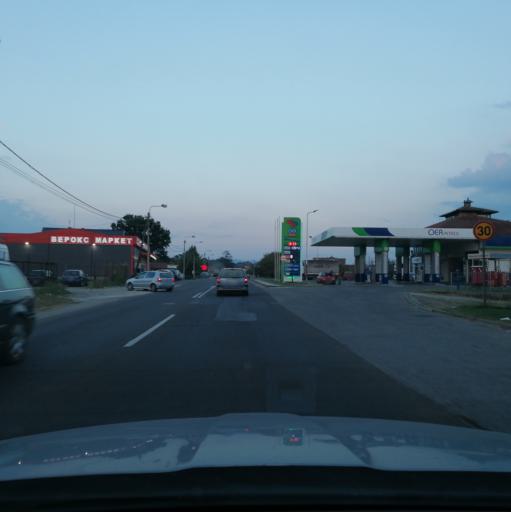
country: RS
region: Central Serbia
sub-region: Raski Okrug
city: Kraljevo
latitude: 43.7030
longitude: 20.7247
